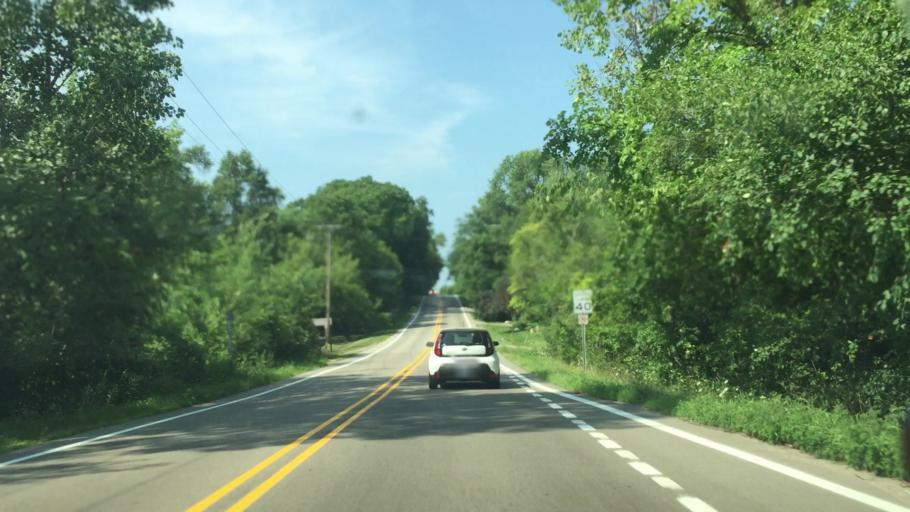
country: US
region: Michigan
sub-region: Oakland County
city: Franklin
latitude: 42.5530
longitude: -83.3026
